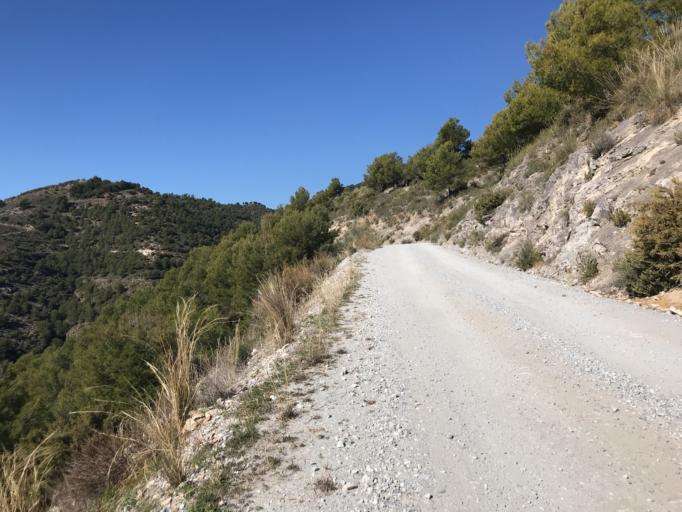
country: ES
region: Andalusia
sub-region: Provincia de Malaga
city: Canillas de Albaida
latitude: 36.8577
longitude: -3.9876
